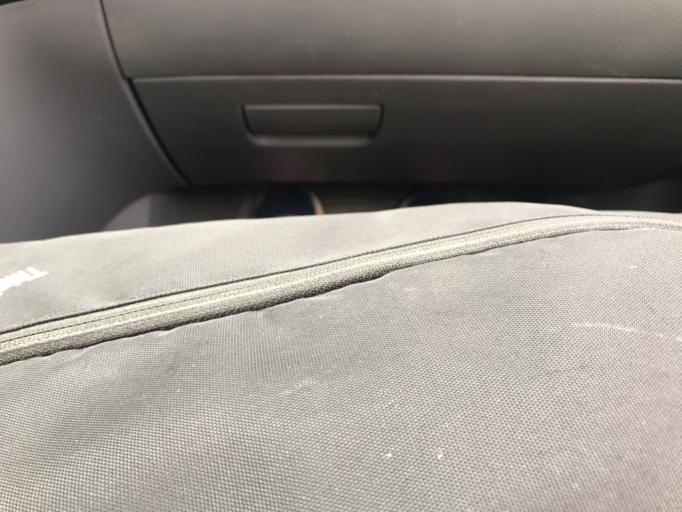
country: TN
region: Zaghwan
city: El Fahs
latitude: 36.2636
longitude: 9.7884
